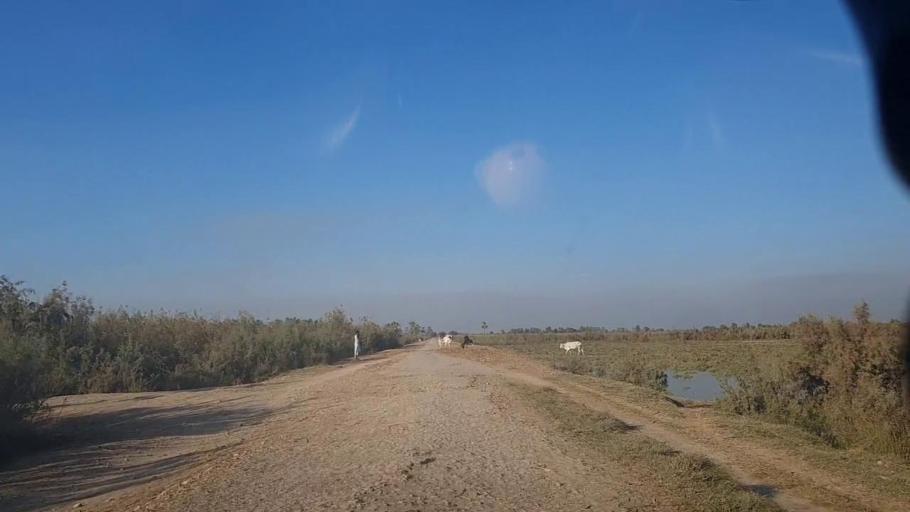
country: PK
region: Sindh
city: Sobhadero
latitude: 27.4045
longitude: 68.4219
